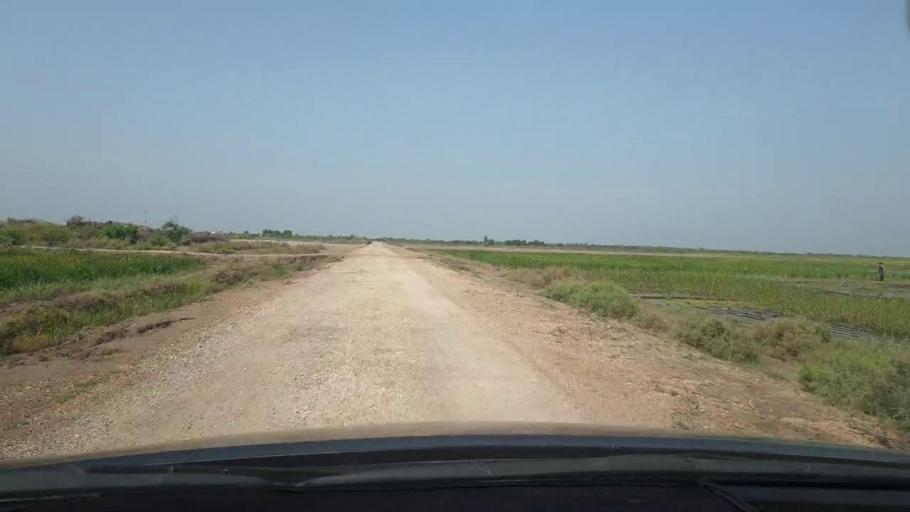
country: PK
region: Sindh
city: Tando Bago
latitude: 24.7179
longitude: 69.1118
